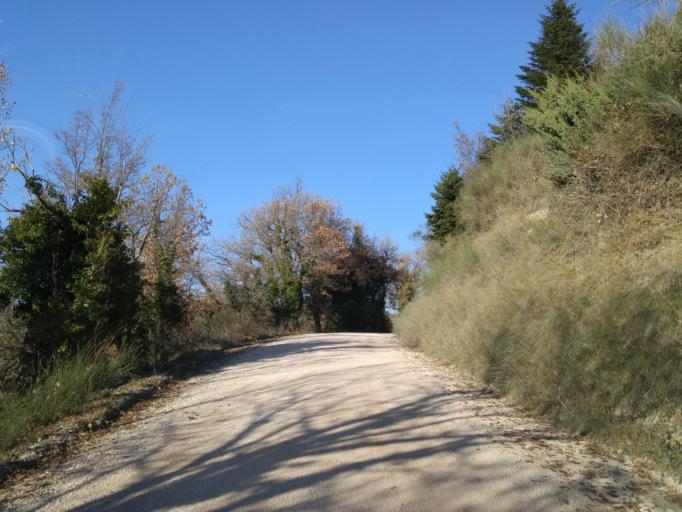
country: IT
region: The Marches
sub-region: Provincia di Pesaro e Urbino
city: Montefelcino
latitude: 43.7686
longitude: 12.8125
